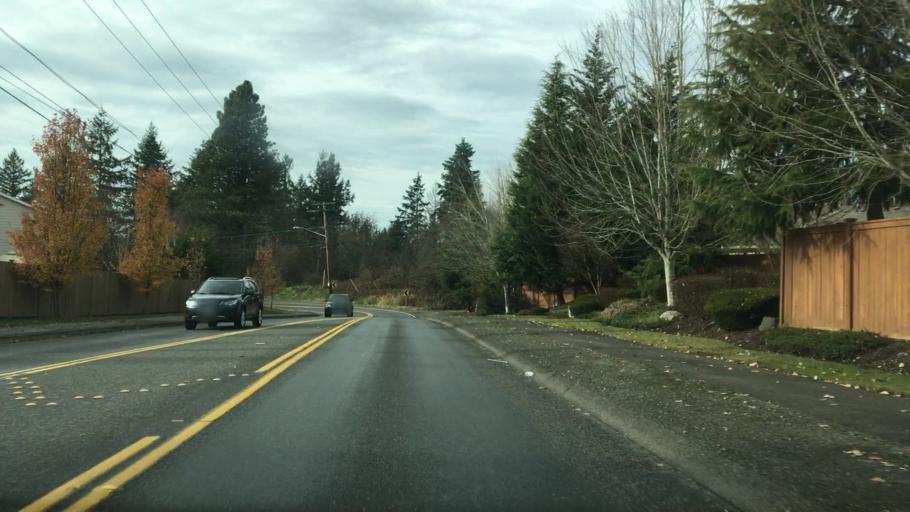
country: US
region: Washington
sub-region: Pierce County
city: Frederickson
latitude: 47.1187
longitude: -122.3233
